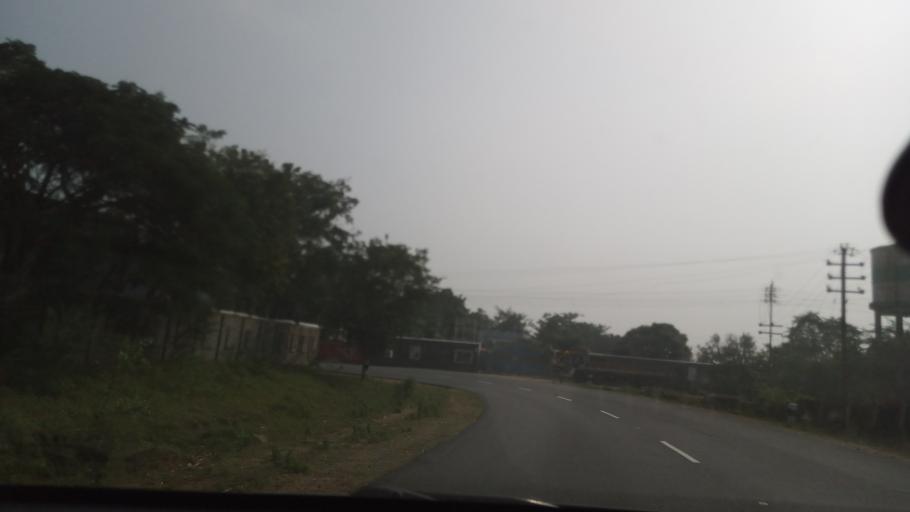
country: IN
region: Tamil Nadu
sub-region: Erode
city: Punjai Puliyampatti
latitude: 11.3997
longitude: 77.1883
